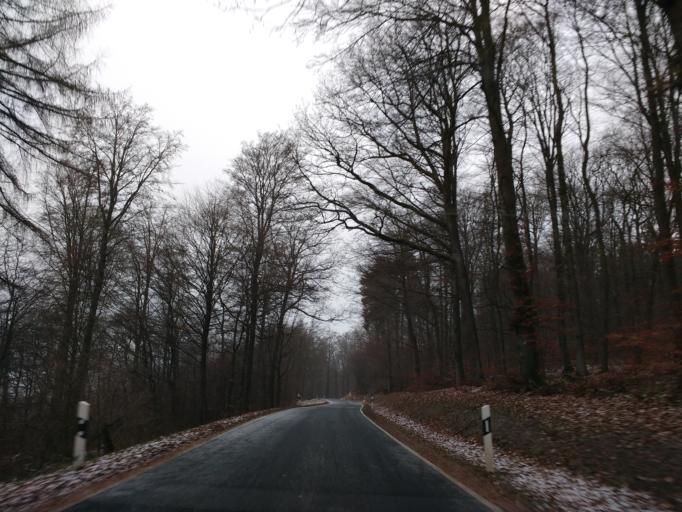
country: DE
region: Hesse
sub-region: Regierungsbezirk Kassel
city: Cornberg
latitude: 51.0827
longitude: 9.7818
